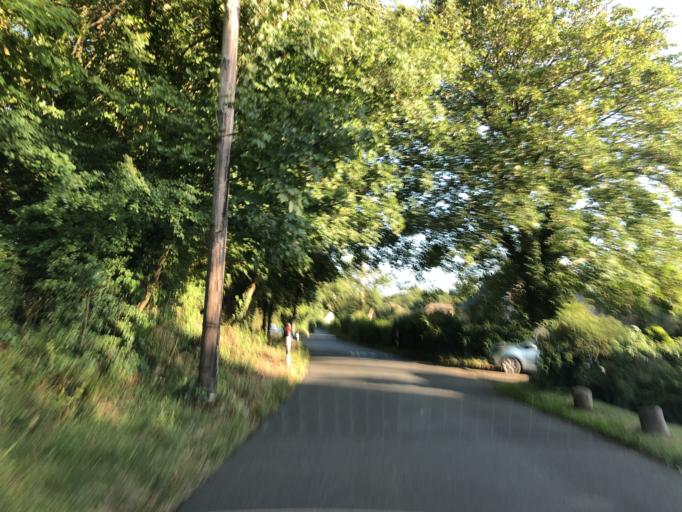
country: GB
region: England
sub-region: Isle of Wight
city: Shalfleet
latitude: 50.6537
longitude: -1.4001
